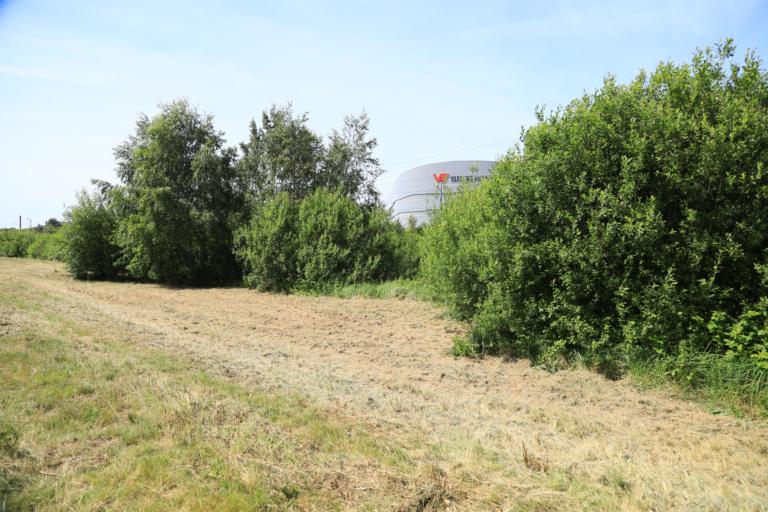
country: SE
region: Halland
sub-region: Varbergs Kommun
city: Varberg
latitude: 57.1211
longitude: 12.2556
